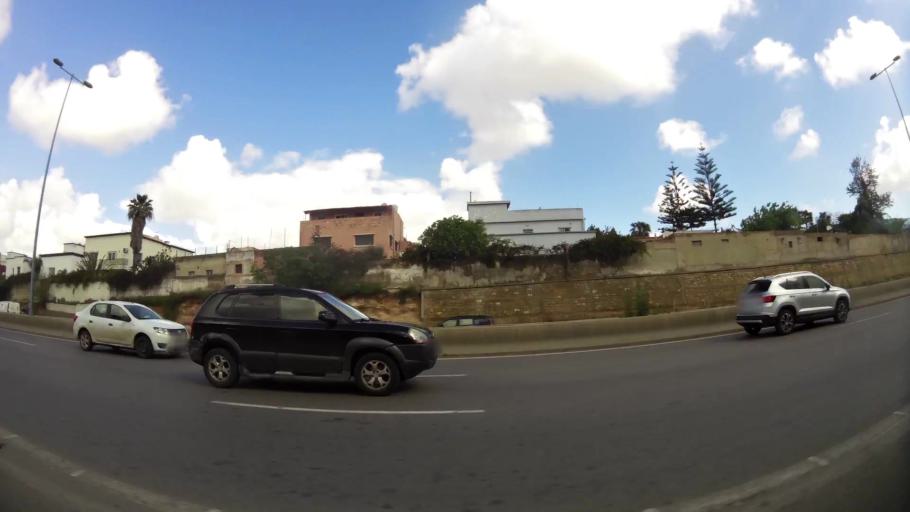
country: MA
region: Grand Casablanca
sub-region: Casablanca
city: Casablanca
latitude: 33.5540
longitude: -7.6212
